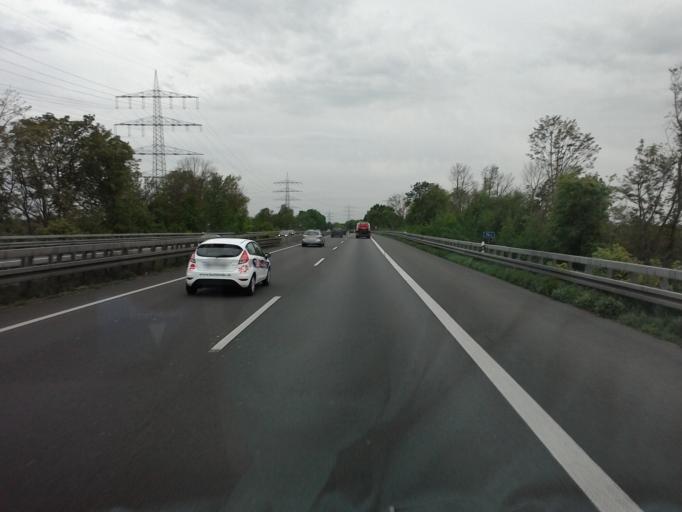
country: DE
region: North Rhine-Westphalia
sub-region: Regierungsbezirk Dusseldorf
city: Dormagen
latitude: 51.1102
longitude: 6.8001
